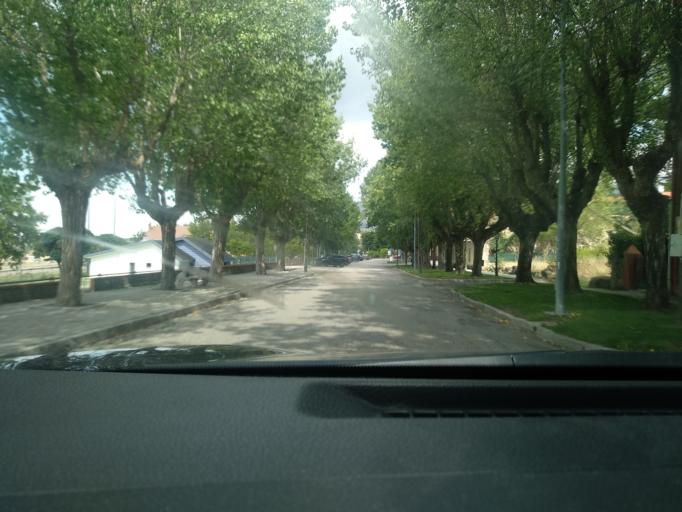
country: ES
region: Castille and Leon
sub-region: Provincia de Segovia
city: Otero de Herreros
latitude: 40.7386
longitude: -4.1879
